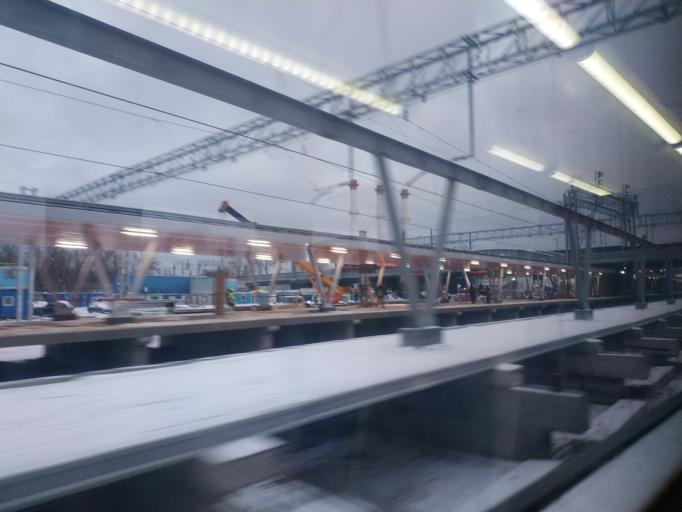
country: RU
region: Moscow
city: Tekstil'shchiki
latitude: 55.7333
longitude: 37.7273
